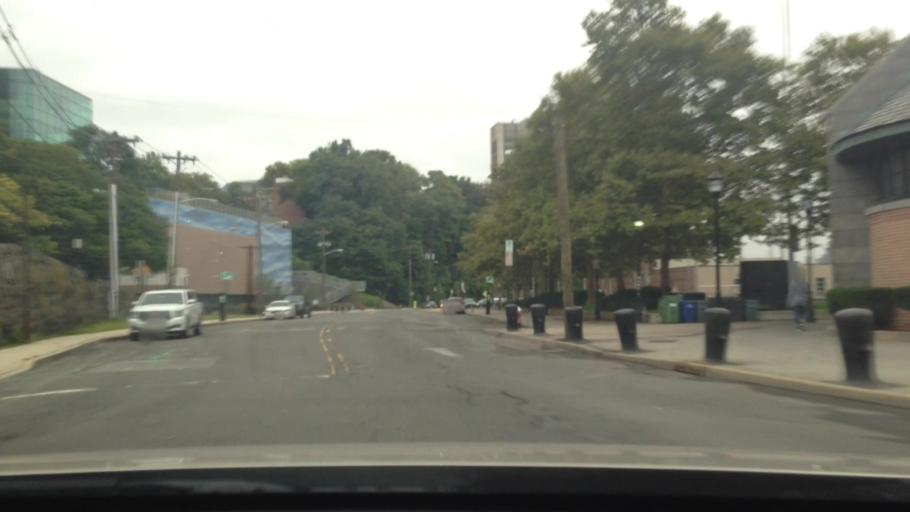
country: US
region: New Jersey
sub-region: Hudson County
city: Hoboken
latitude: 40.7414
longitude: -74.0265
